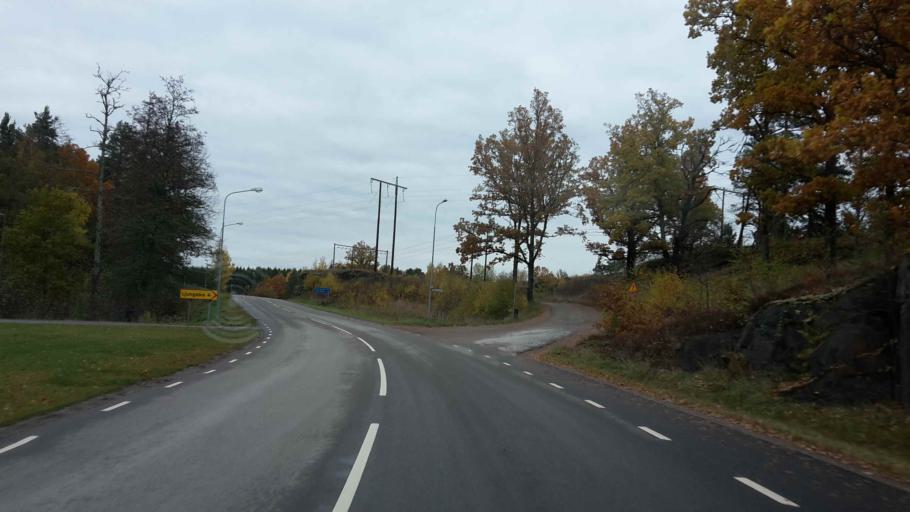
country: SE
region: OEstergoetland
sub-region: Atvidabergs Kommun
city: Atvidaberg
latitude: 58.2112
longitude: 16.0122
